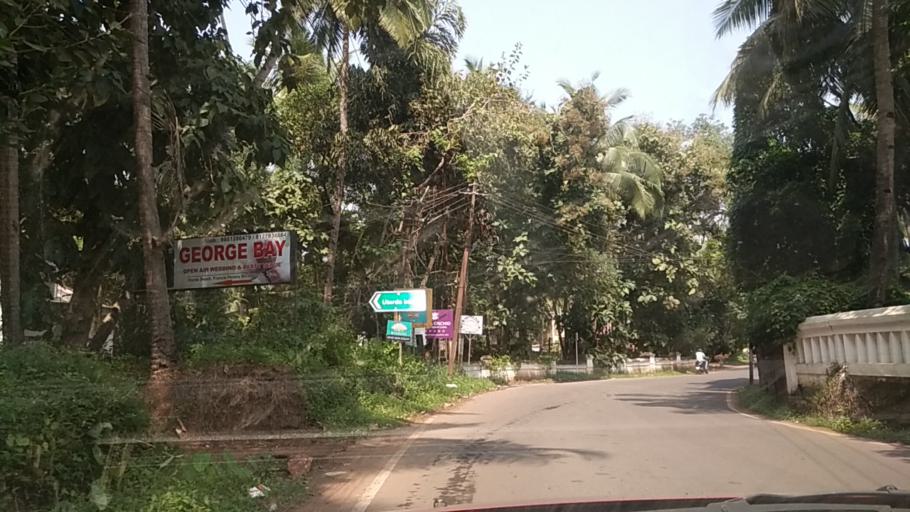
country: IN
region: Goa
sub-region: South Goa
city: Colva
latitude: 15.3213
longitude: 73.9061
